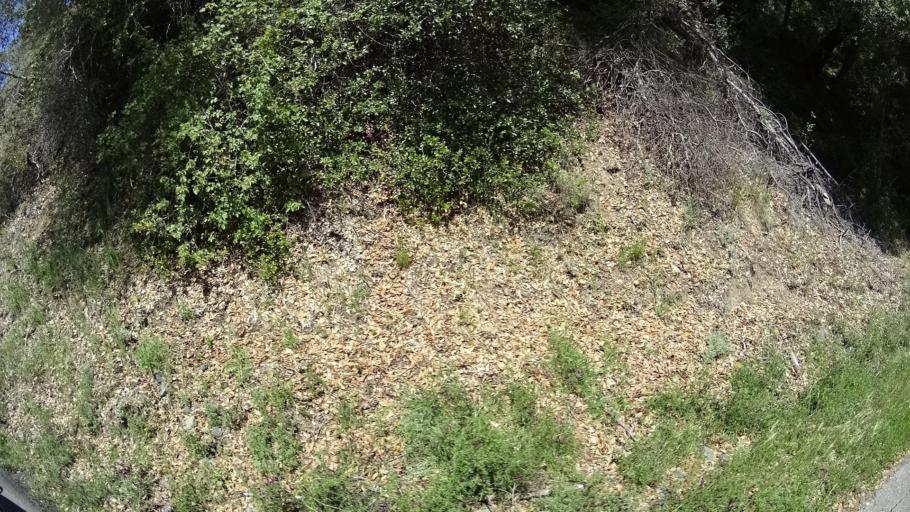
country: US
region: California
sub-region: Humboldt County
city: Redway
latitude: 40.2228
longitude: -123.6040
